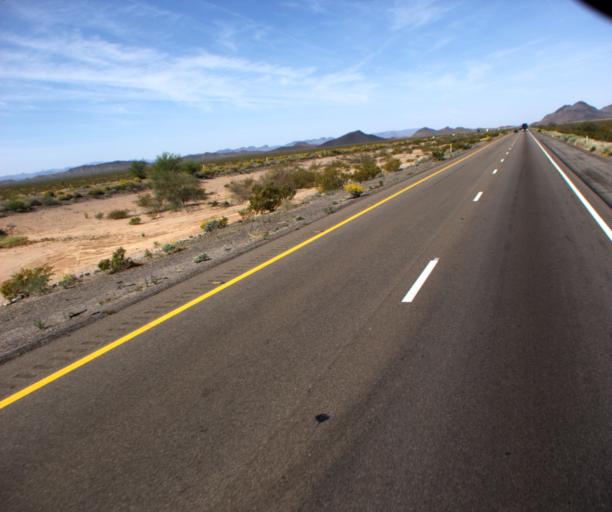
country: US
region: Arizona
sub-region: La Paz County
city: Salome
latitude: 33.6008
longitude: -113.5627
